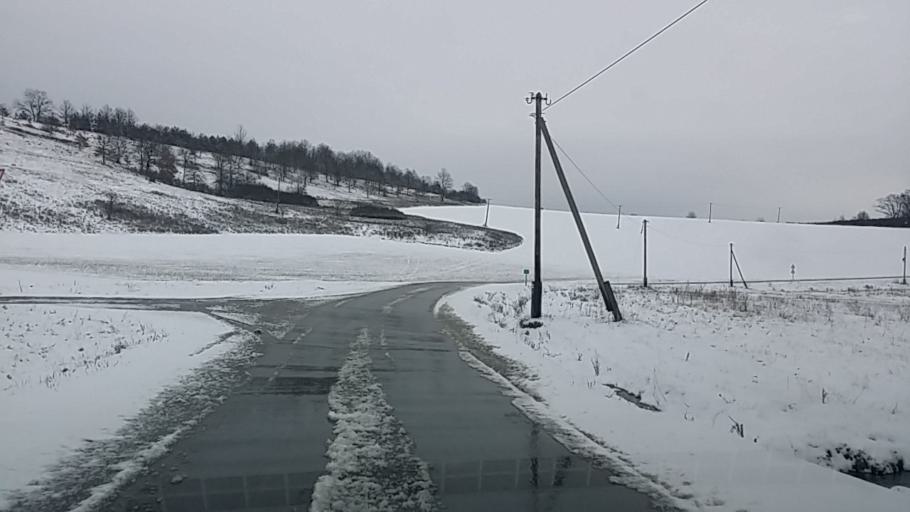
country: HU
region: Borsod-Abauj-Zemplen
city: Rudabanya
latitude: 48.4471
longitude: 20.6567
